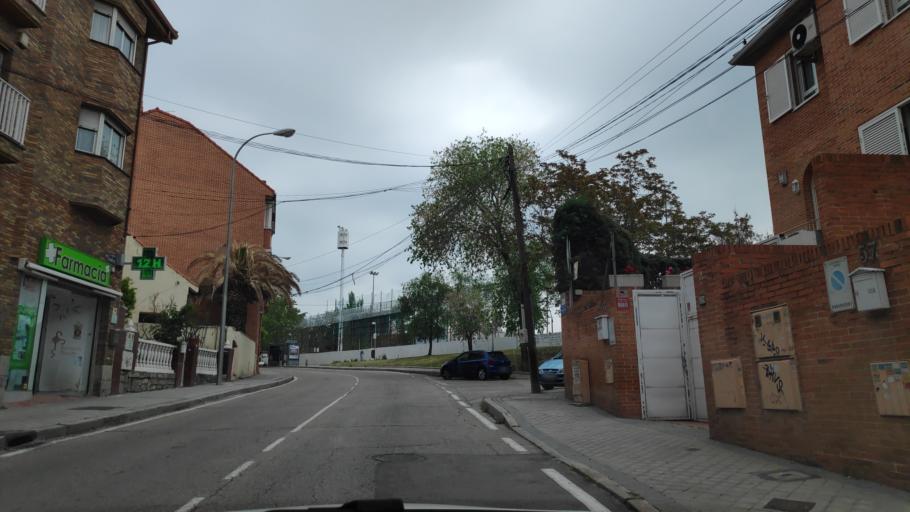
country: ES
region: Madrid
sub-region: Provincia de Madrid
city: Pozuelo de Alarcon
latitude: 40.4575
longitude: -3.7795
